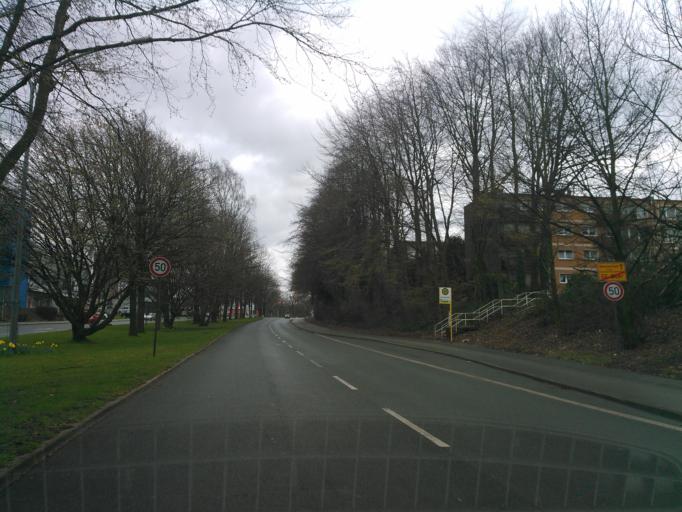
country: DE
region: North Rhine-Westphalia
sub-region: Regierungsbezirk Munster
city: Gladbeck
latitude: 51.5858
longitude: 7.0509
